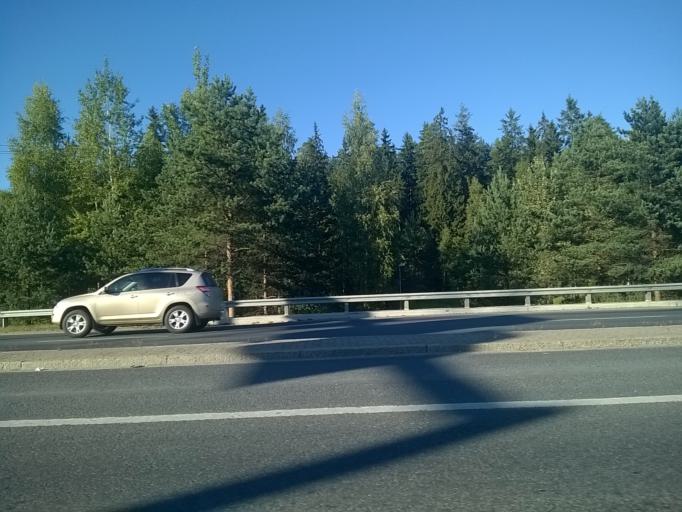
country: FI
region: Pirkanmaa
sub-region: Tampere
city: Tampere
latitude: 61.5000
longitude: 23.8766
